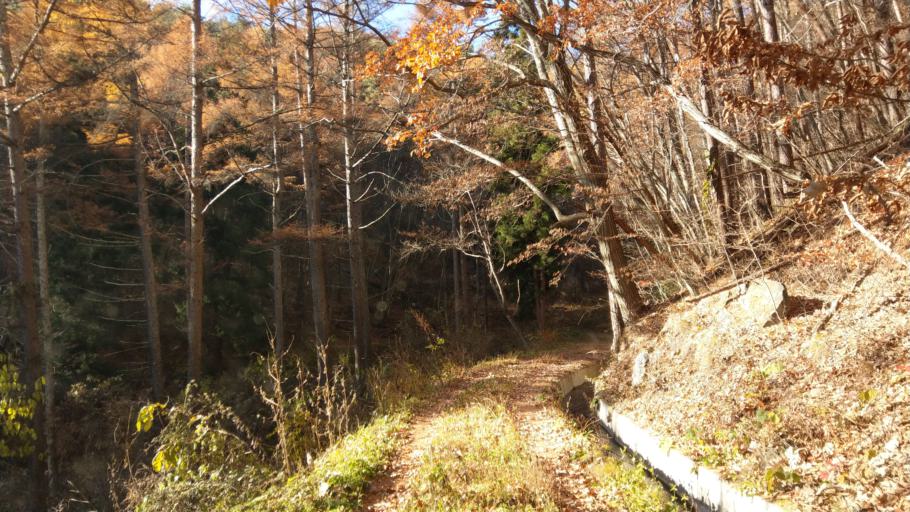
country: JP
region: Nagano
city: Komoro
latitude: 36.3622
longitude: 138.4354
